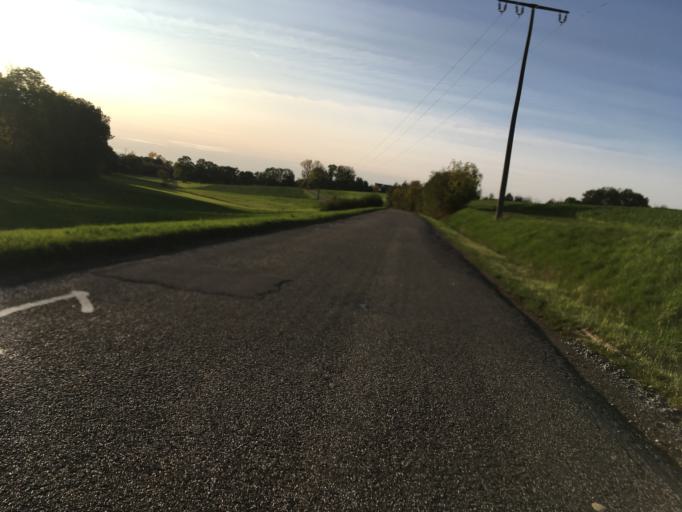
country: DE
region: Baden-Wuerttemberg
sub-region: Regierungsbezirk Stuttgart
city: Neuenstein
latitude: 49.2208
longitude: 9.5987
